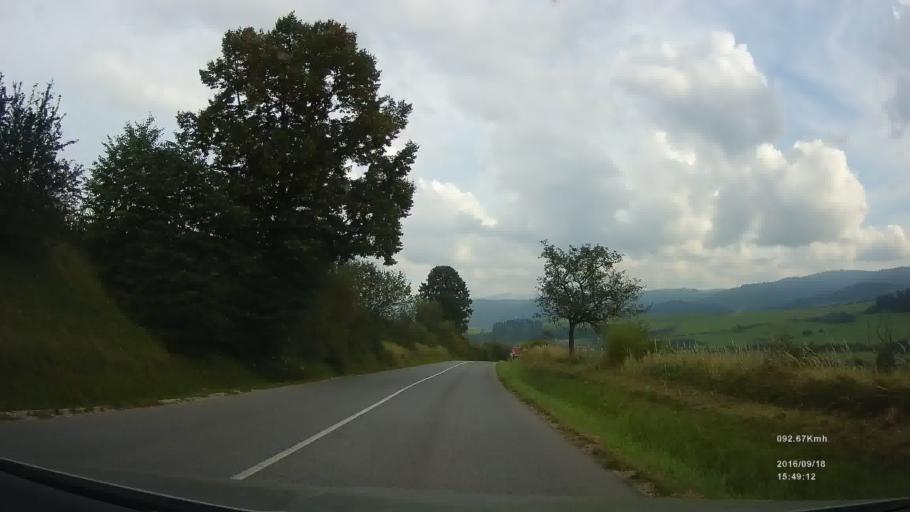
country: SK
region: Kosicky
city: Spisska Nova Ves
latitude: 48.9195
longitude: 20.6058
